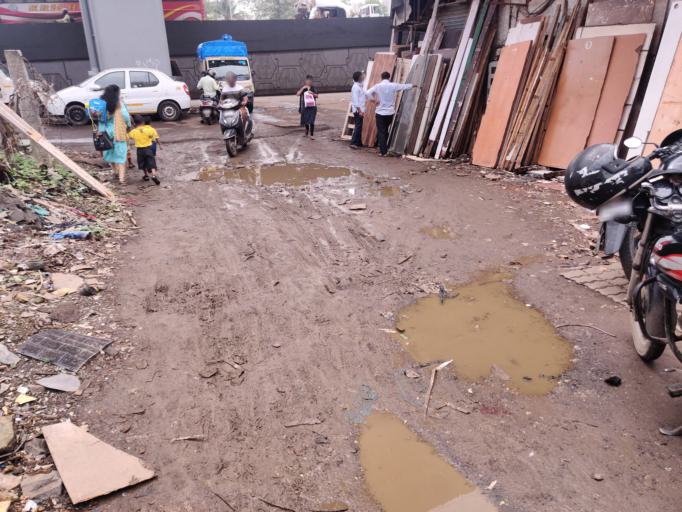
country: IN
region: Maharashtra
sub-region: Mumbai Suburban
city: Borivli
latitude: 19.2457
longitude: 72.8643
